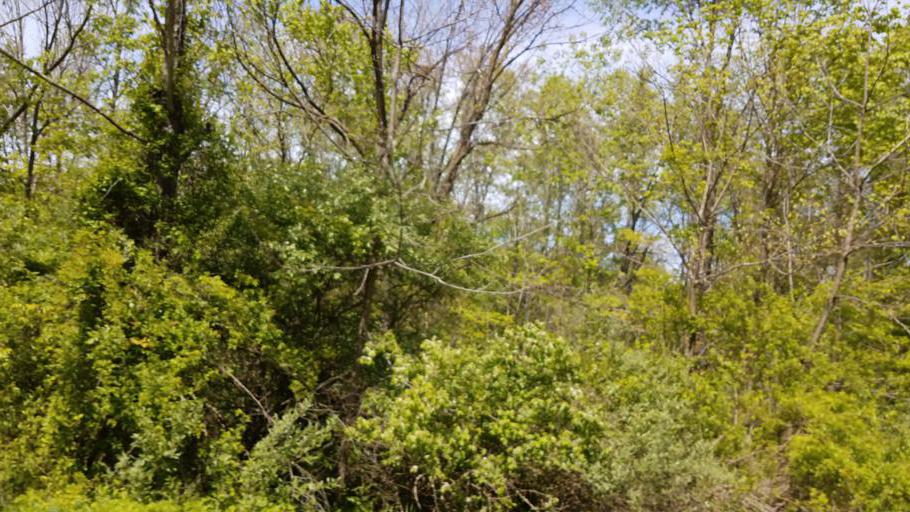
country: US
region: Ohio
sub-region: Knox County
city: Gambier
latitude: 40.4163
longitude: -82.3619
